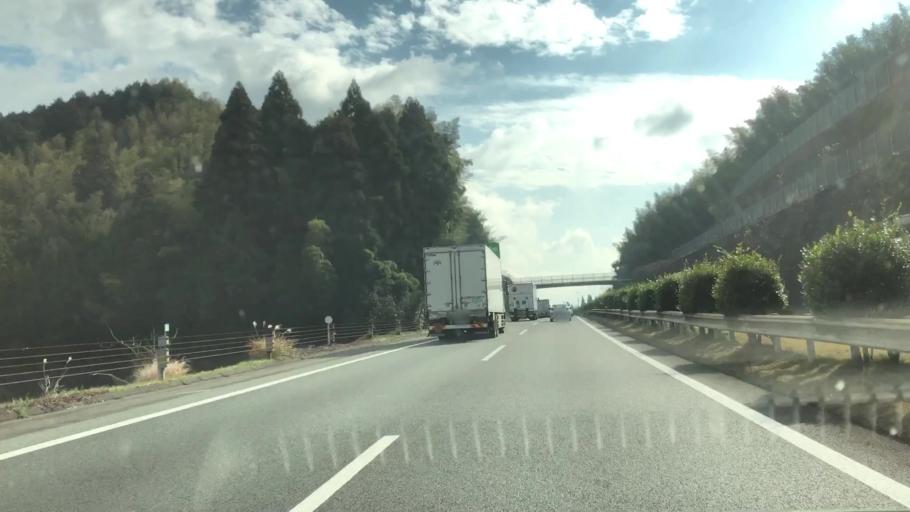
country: JP
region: Fukuoka
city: Setakamachi-takayanagi
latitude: 33.0916
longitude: 130.5387
